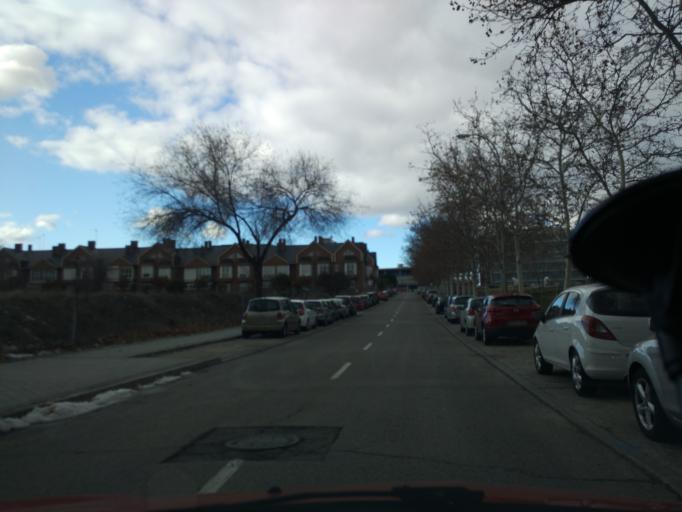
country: ES
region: Madrid
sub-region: Provincia de Madrid
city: San Blas
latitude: 40.4454
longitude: -3.6323
